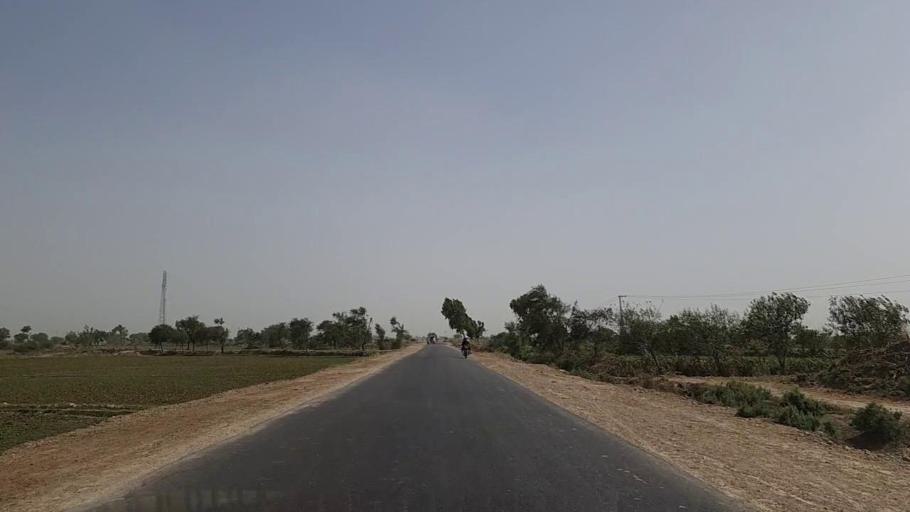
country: PK
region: Sindh
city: Tando Bago
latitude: 24.8286
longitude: 68.8953
